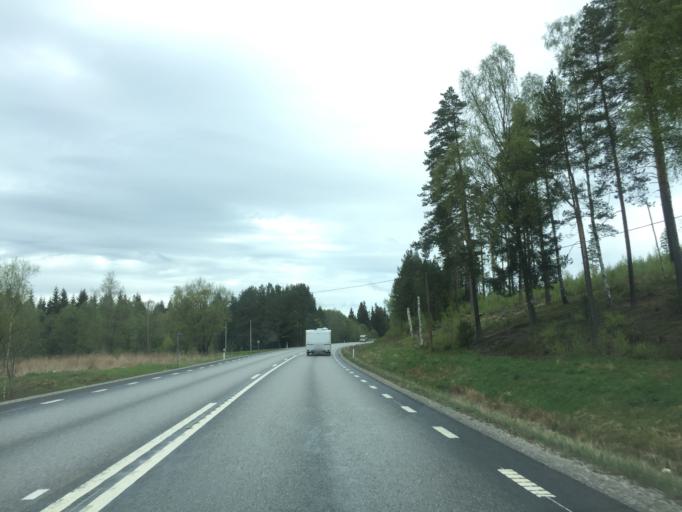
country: SE
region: OErebro
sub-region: Lindesbergs Kommun
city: Lindesberg
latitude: 59.6063
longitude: 15.1847
